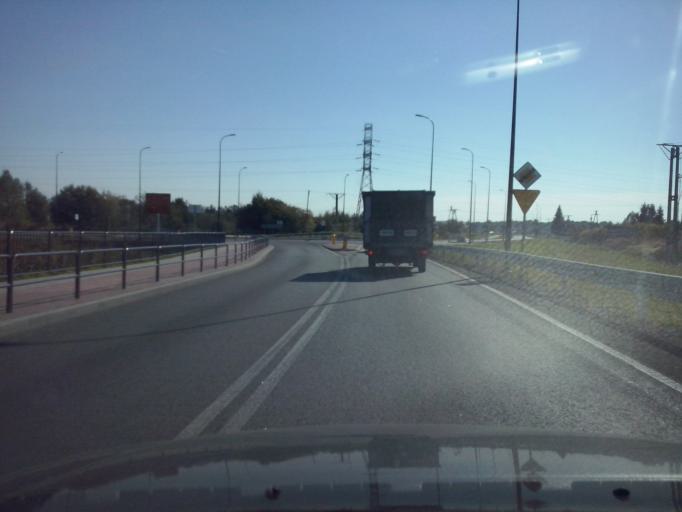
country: PL
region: Lublin Voivodeship
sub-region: Powiat bilgorajski
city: Bilgoraj
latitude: 50.5470
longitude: 22.7039
